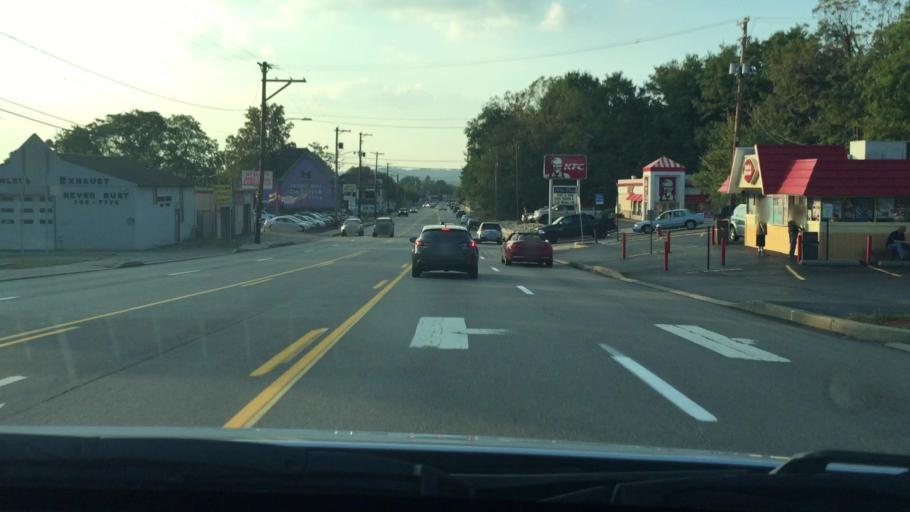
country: US
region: Pennsylvania
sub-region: Allegheny County
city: Bellevue
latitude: 40.4876
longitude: -80.0560
